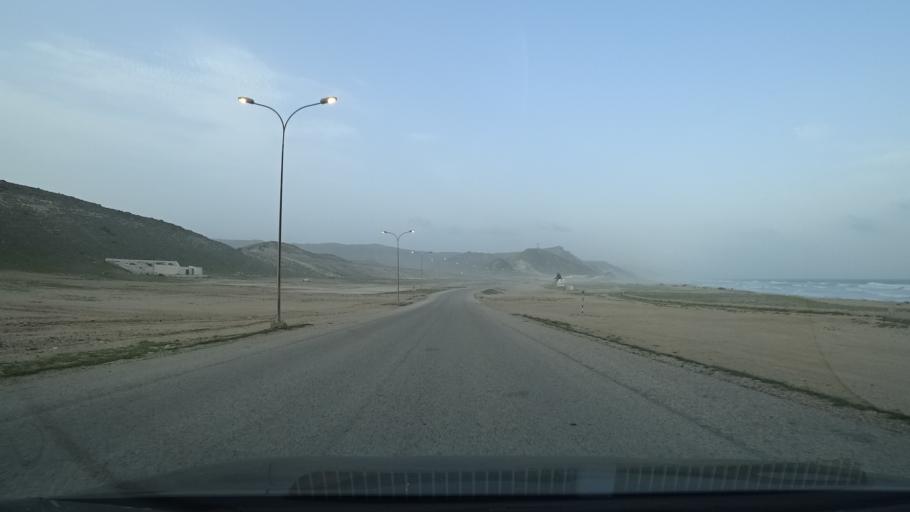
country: OM
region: Zufar
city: Salalah
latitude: 16.8781
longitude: 53.7688
